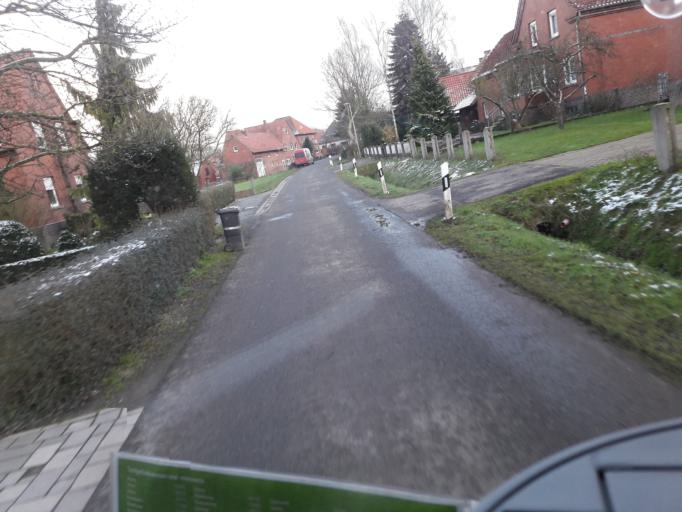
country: DE
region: Lower Saxony
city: Buckeburg
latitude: 52.2361
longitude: 9.0575
